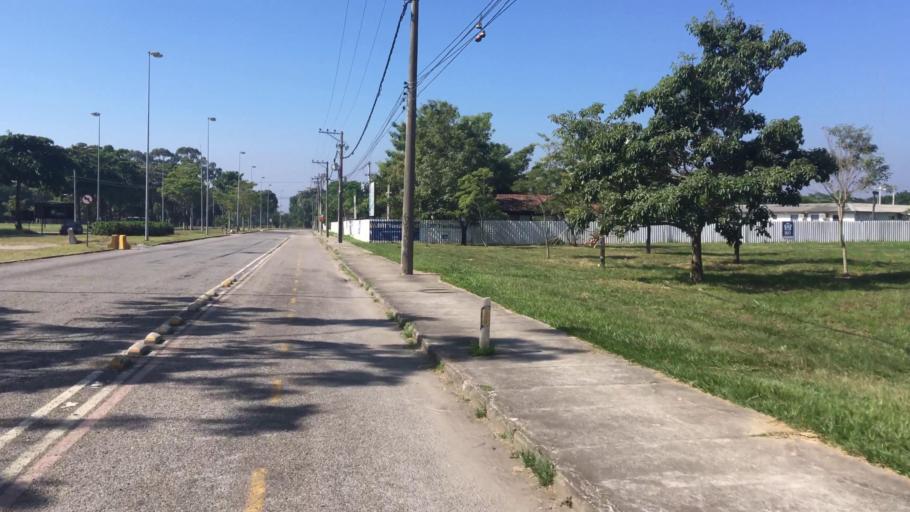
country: BR
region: Rio de Janeiro
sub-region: Rio De Janeiro
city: Rio de Janeiro
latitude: -22.8413
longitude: -43.2307
